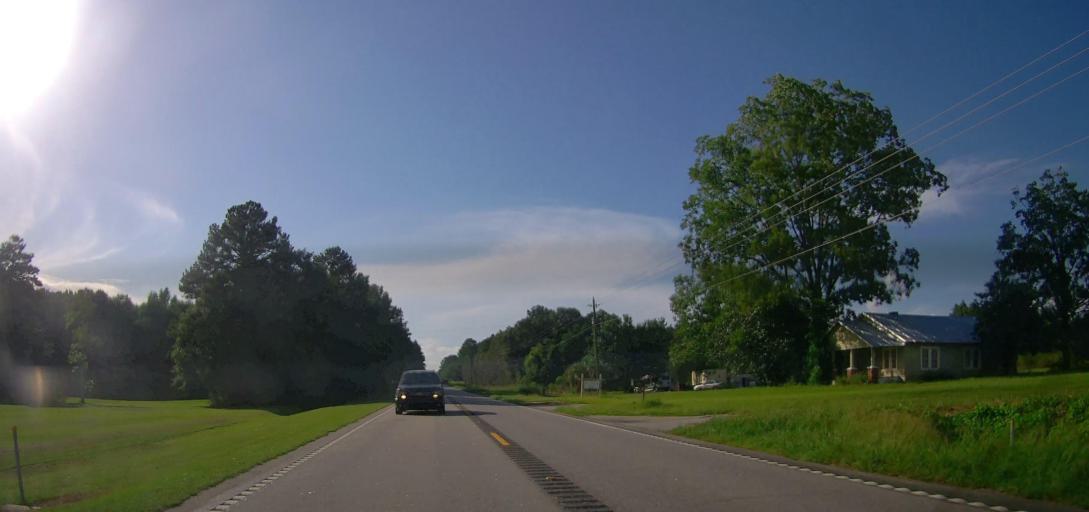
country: US
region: Georgia
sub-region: Coffee County
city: Nicholls
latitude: 31.4064
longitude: -82.6774
